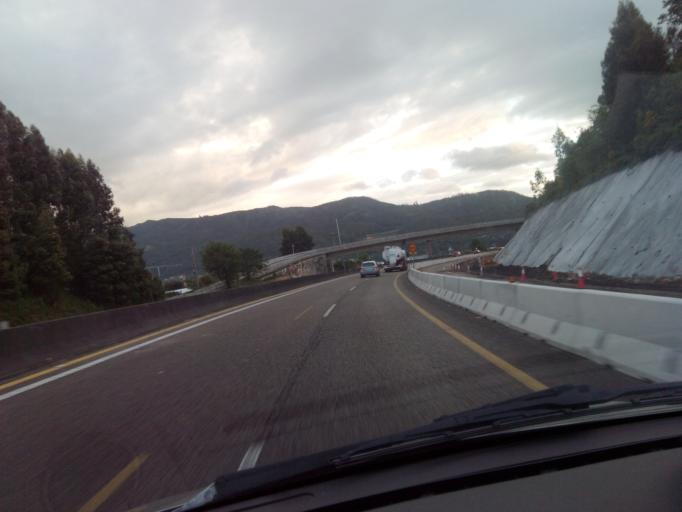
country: ES
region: Galicia
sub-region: Provincia de Pontevedra
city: Redondela
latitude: 42.2750
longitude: -8.6659
